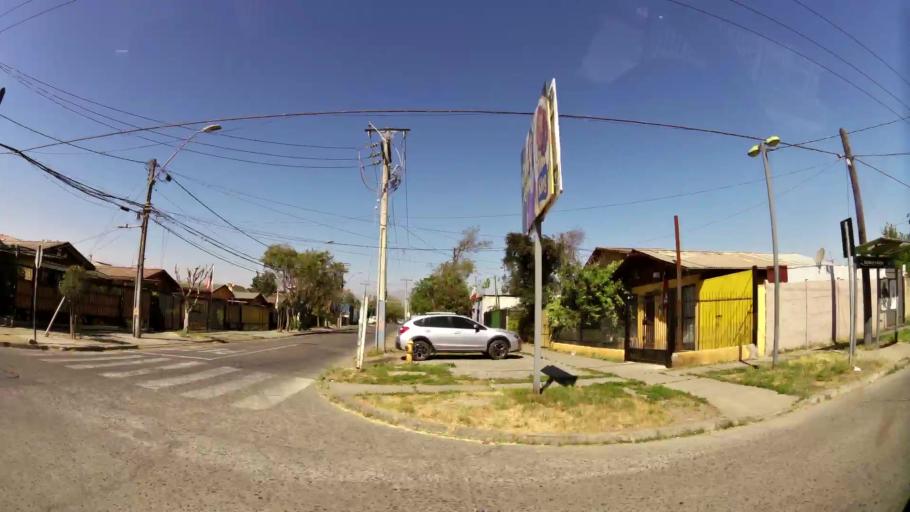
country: CL
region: Santiago Metropolitan
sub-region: Provincia de Maipo
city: San Bernardo
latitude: -33.6000
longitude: -70.7130
